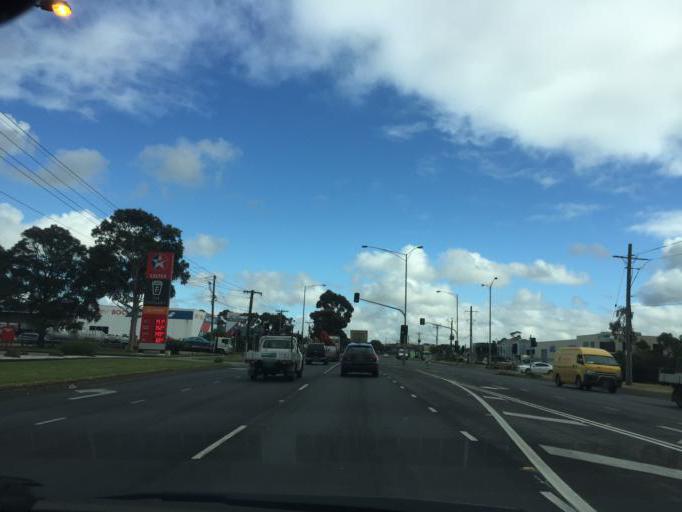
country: AU
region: Victoria
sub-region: Brimbank
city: Brooklyn
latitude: -37.8194
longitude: 144.8197
